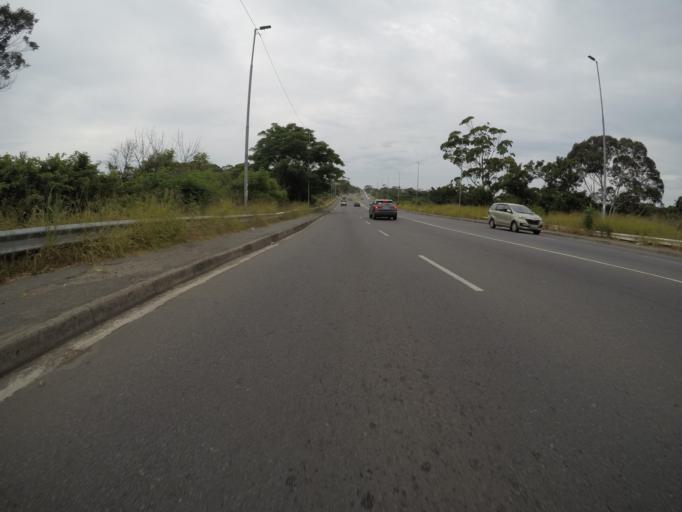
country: ZA
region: Eastern Cape
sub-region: Buffalo City Metropolitan Municipality
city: East London
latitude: -32.9976
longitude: 27.8800
